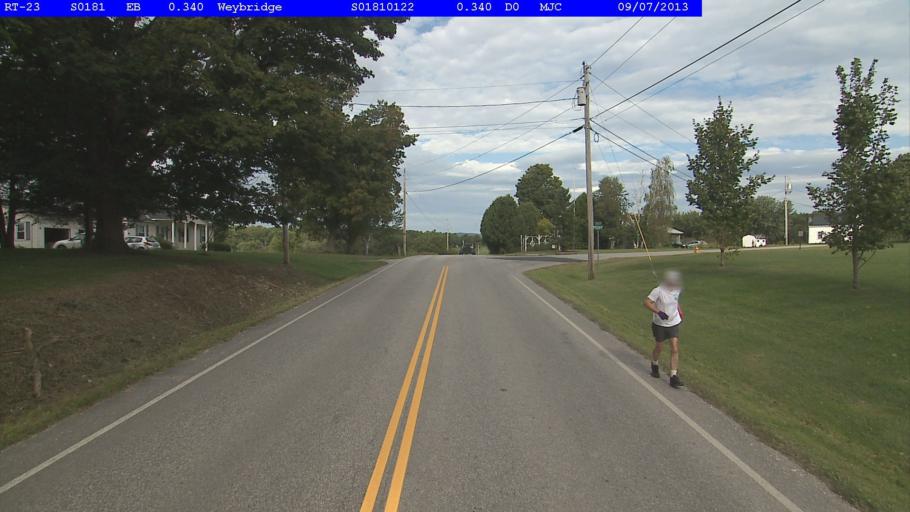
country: US
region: Vermont
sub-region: Addison County
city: Middlebury (village)
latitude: 44.0219
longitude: -73.1880
